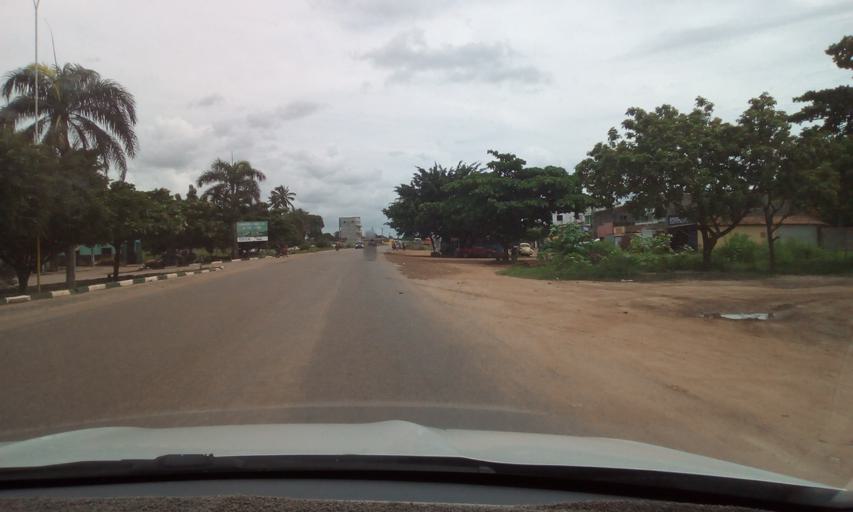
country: BR
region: Paraiba
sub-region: Mari
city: Mari
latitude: -7.0531
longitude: -35.3192
